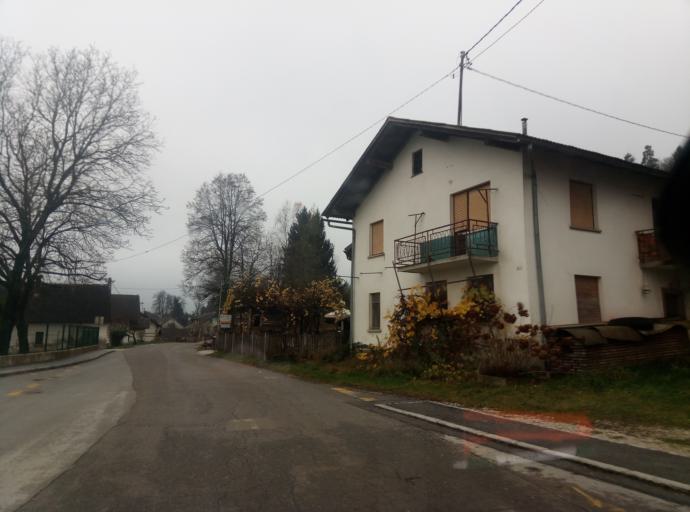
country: SI
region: Vodice
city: Vodice
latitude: 46.1713
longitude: 14.4810
